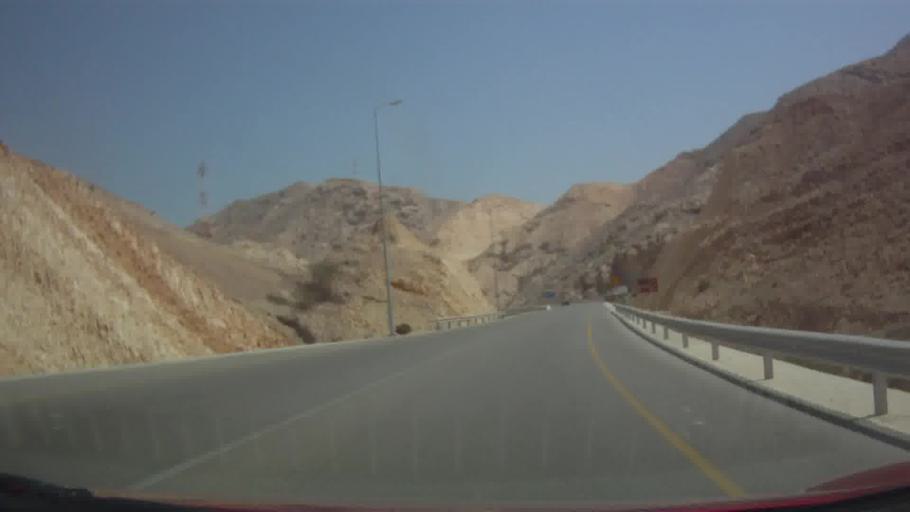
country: OM
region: Muhafazat Masqat
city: Muscat
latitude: 23.5412
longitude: 58.6427
